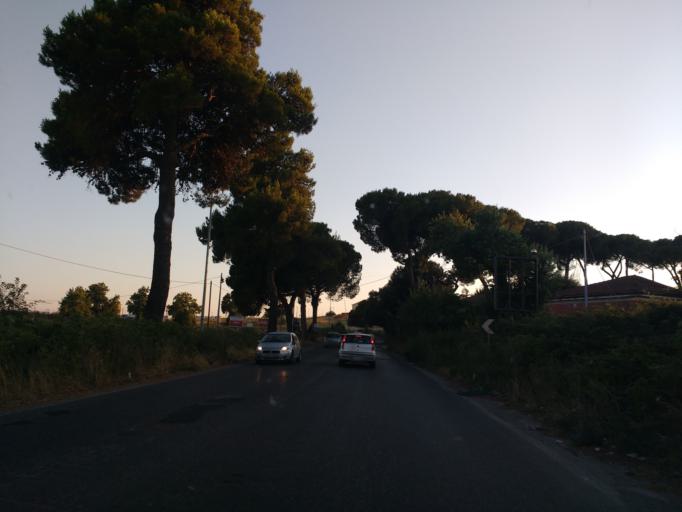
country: IT
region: Latium
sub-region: Citta metropolitana di Roma Capitale
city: Albuccione
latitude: 41.9515
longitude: 12.6868
